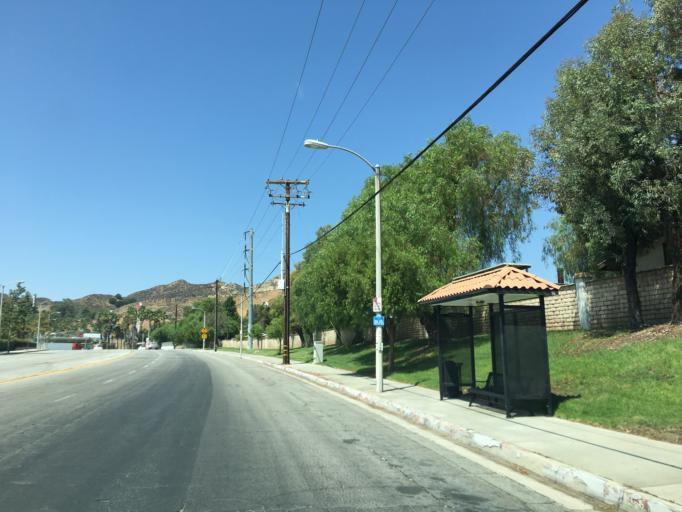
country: US
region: California
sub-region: Los Angeles County
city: Castaic
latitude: 34.4975
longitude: -118.6200
